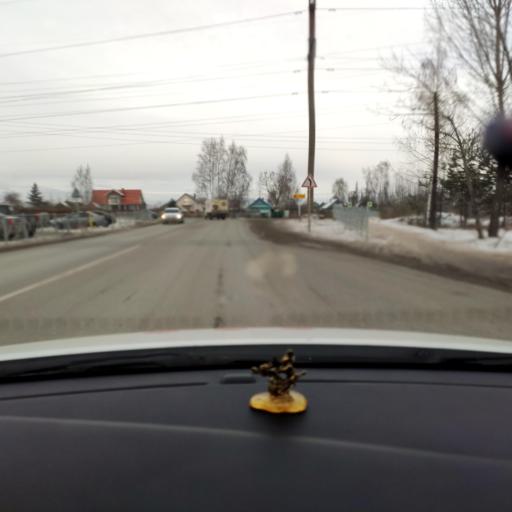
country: RU
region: Tatarstan
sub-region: Zelenodol'skiy Rayon
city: Zelenodolsk
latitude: 55.8672
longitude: 48.5456
